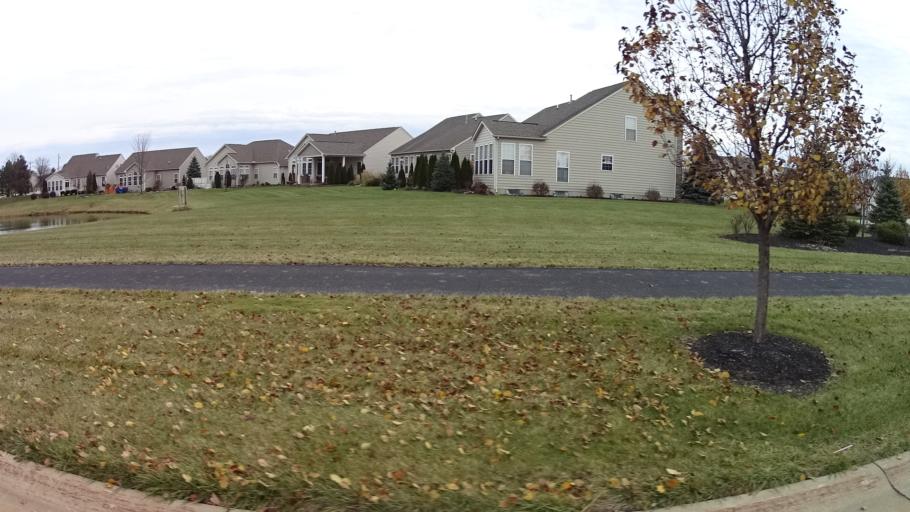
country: US
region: Ohio
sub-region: Lorain County
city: North Ridgeville
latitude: 41.4074
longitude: -82.0416
